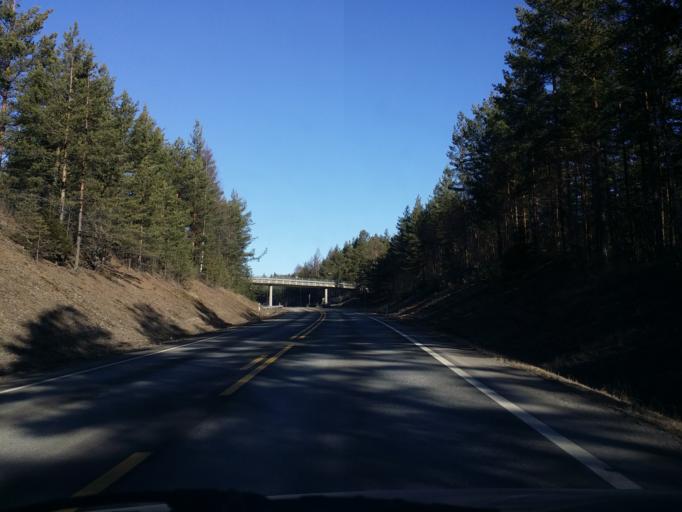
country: NO
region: Buskerud
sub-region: Ringerike
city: Honefoss
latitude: 60.2177
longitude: 10.2588
